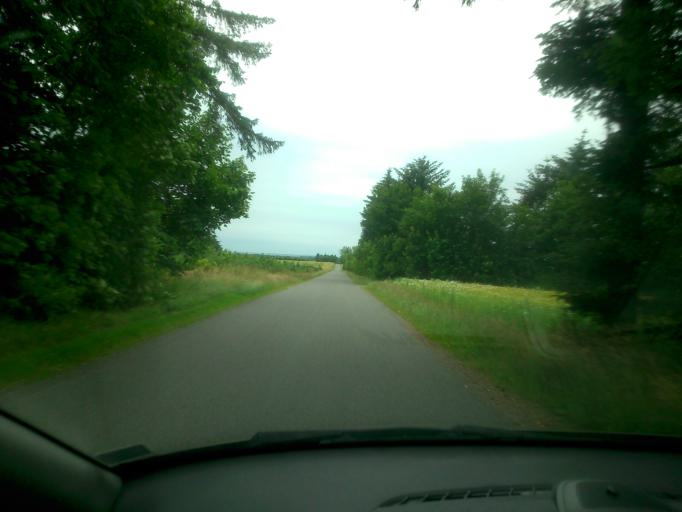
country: DK
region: Central Jutland
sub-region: Ringkobing-Skjern Kommune
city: Skjern
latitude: 55.9789
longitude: 8.4434
